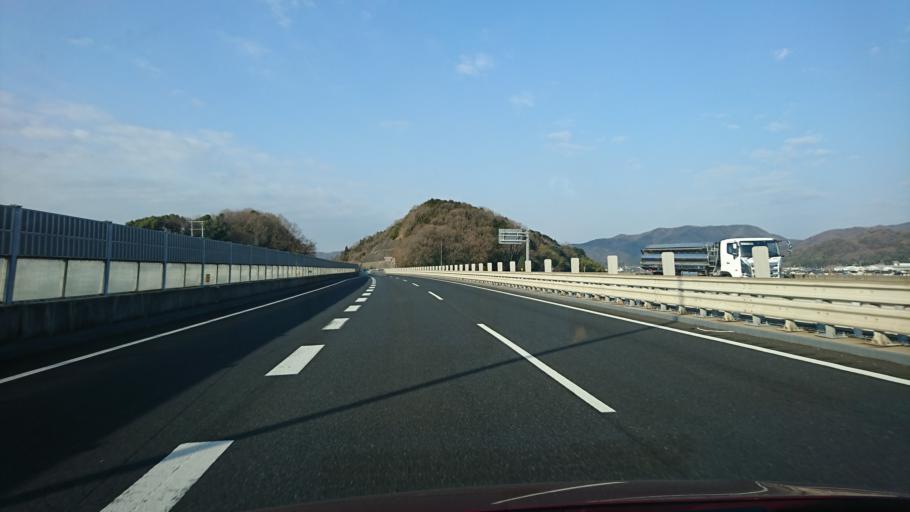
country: JP
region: Hyogo
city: Tatsunocho-tominaga
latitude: 34.8525
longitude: 134.5408
